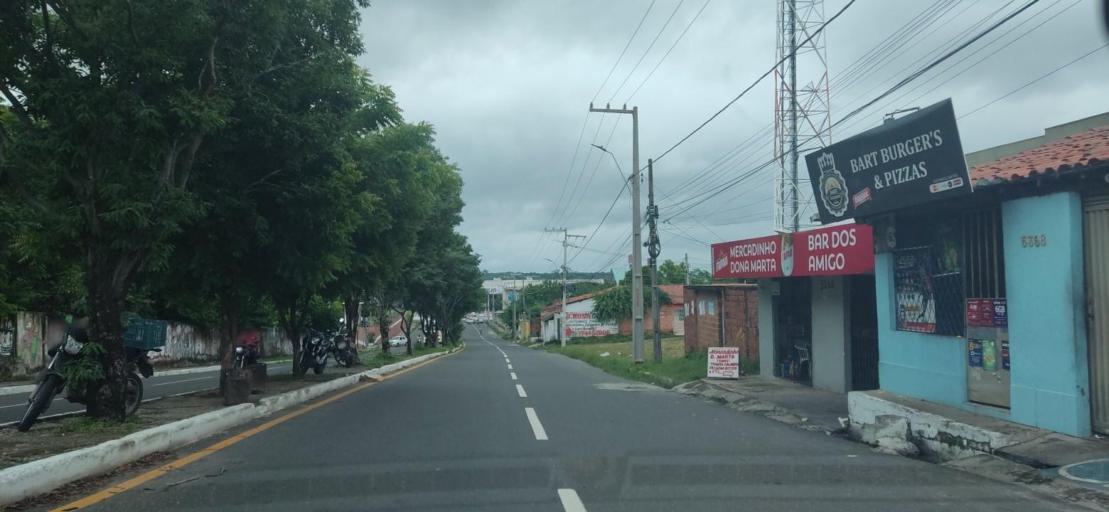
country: BR
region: Piaui
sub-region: Teresina
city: Teresina
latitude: -5.0652
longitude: -42.7513
